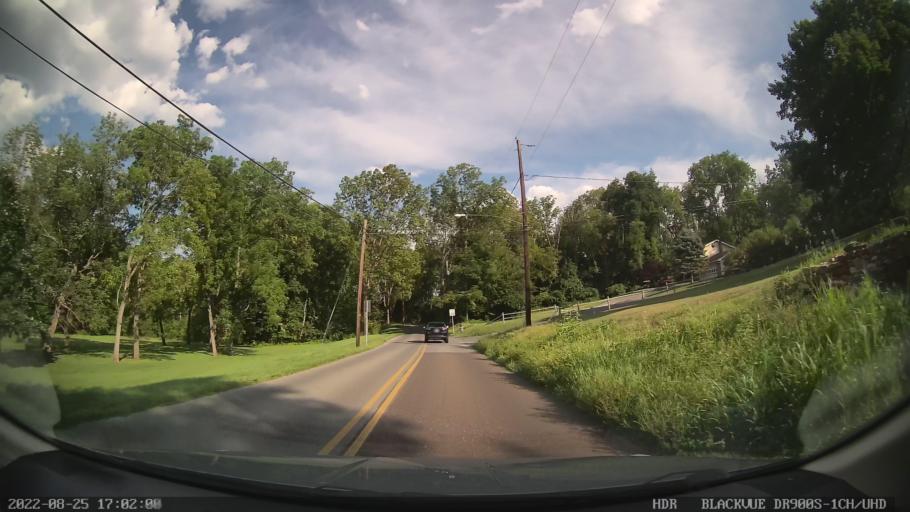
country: US
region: Pennsylvania
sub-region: Lehigh County
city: Emmaus
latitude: 40.5548
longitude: -75.5046
